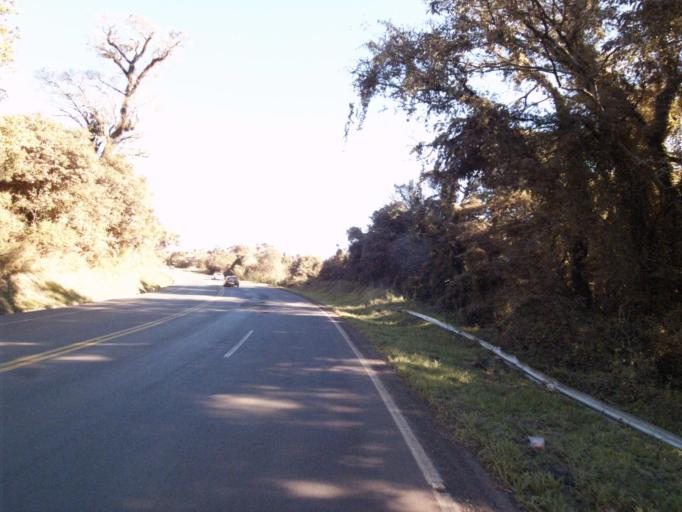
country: BR
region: Santa Catarina
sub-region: Xanxere
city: Xanxere
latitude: -26.9165
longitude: -52.4929
